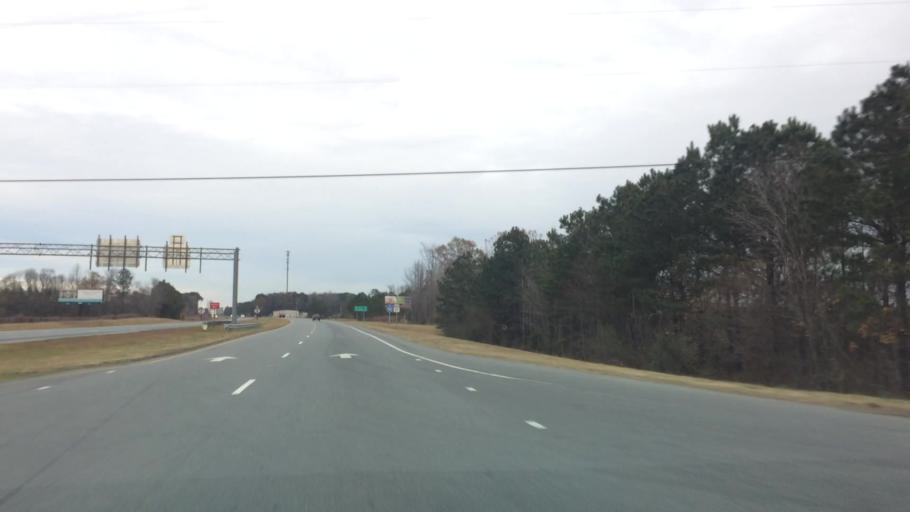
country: US
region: North Carolina
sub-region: Wayne County
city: Mount Olive
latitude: 35.1577
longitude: -78.1110
